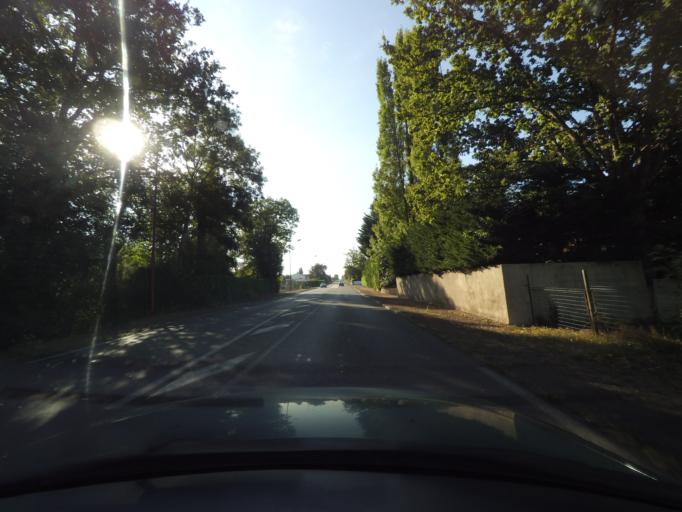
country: FR
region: Poitou-Charentes
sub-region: Departement des Deux-Sevres
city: Boisme
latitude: 46.8253
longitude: -0.4192
